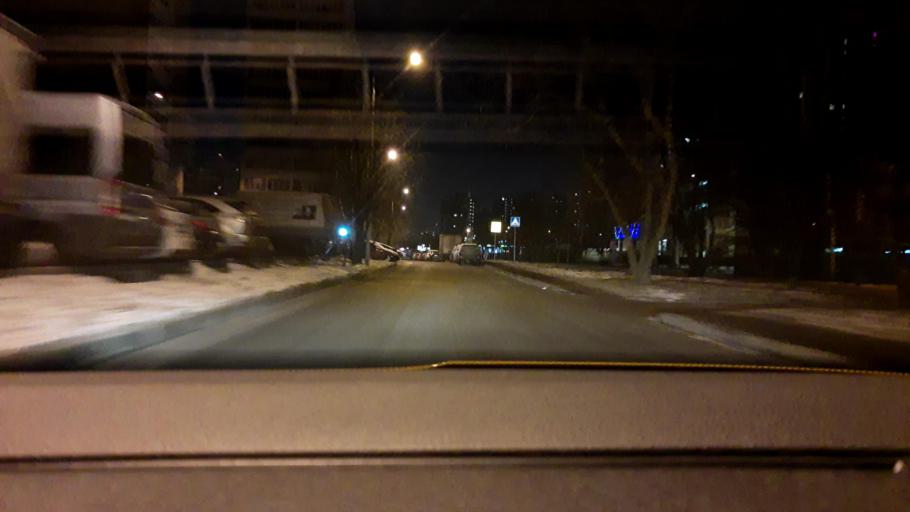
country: RU
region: Moscow
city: Lianozovo
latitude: 55.9004
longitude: 37.5913
